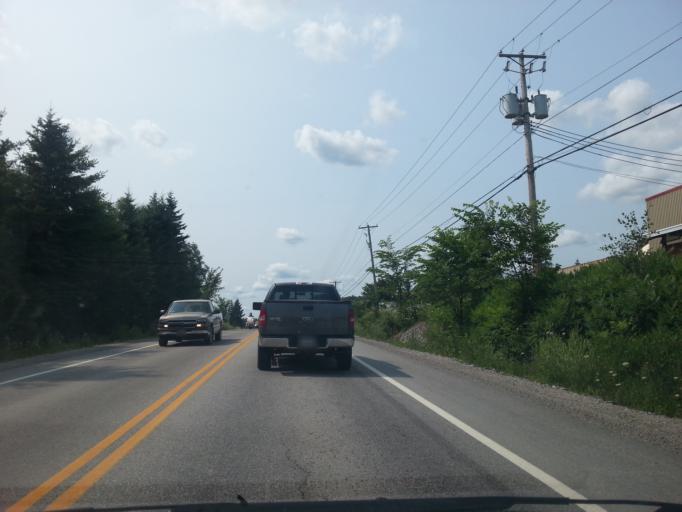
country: CA
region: Quebec
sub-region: Outaouais
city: Wakefield
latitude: 45.6158
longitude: -75.9176
